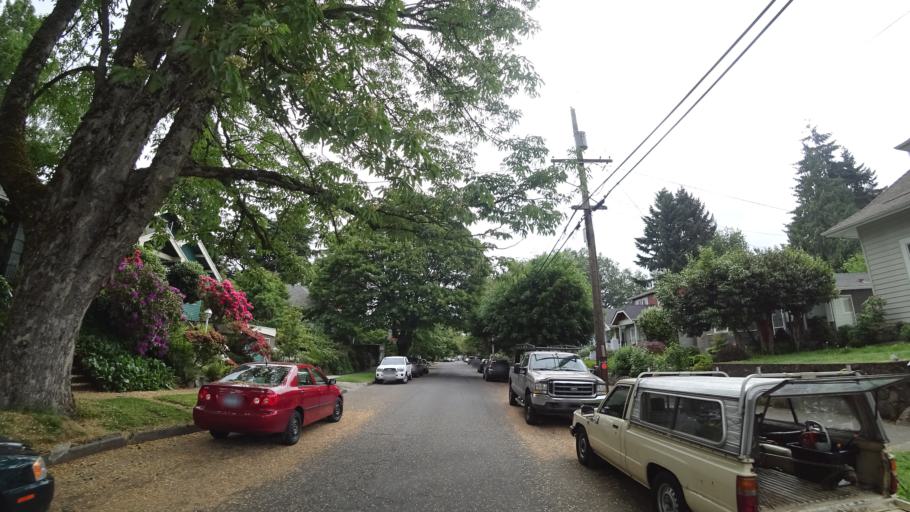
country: US
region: Oregon
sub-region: Multnomah County
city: Portland
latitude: 45.5005
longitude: -122.6299
